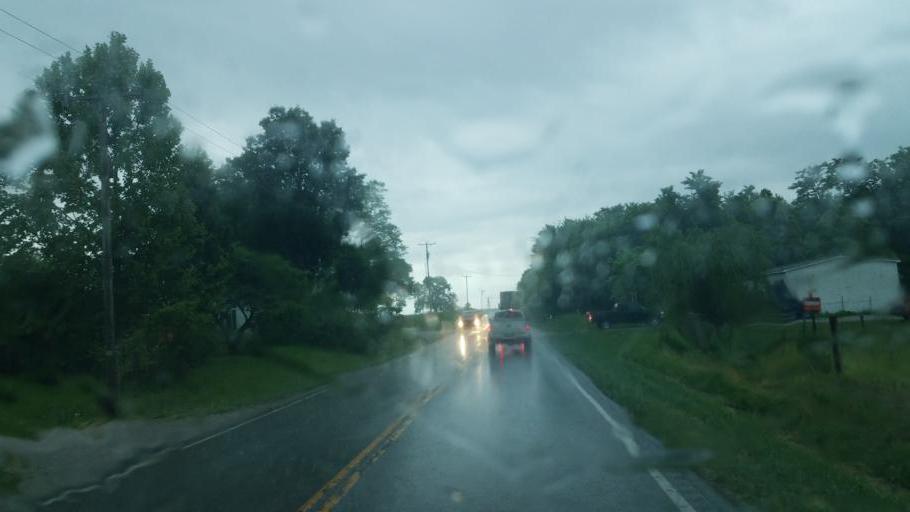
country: US
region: Missouri
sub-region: Cooper County
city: Boonville
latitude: 38.8908
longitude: -92.6548
